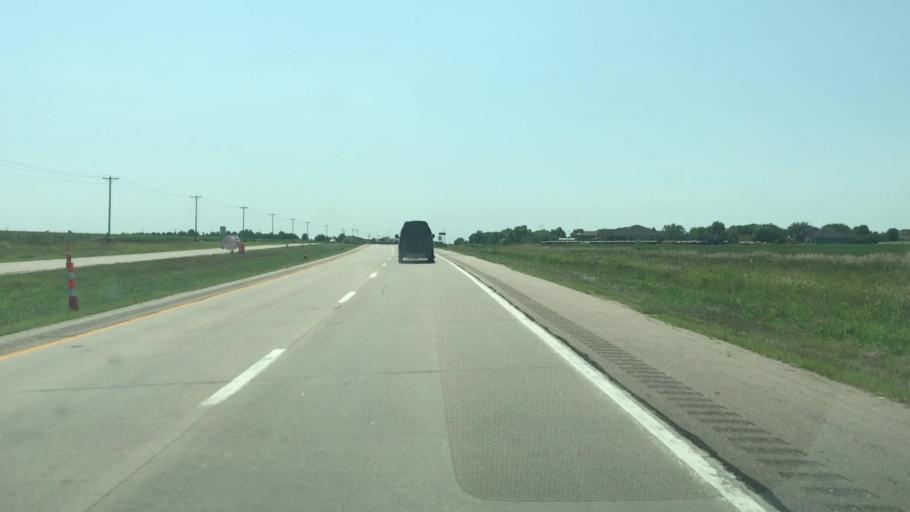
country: US
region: Nebraska
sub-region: Adams County
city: Hastings
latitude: 40.6460
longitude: -98.3824
